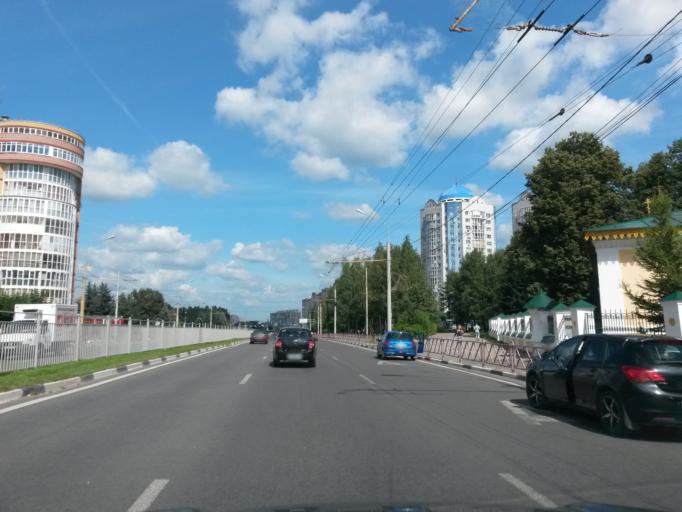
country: RU
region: Jaroslavl
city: Yaroslavl
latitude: 57.5788
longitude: 39.8481
